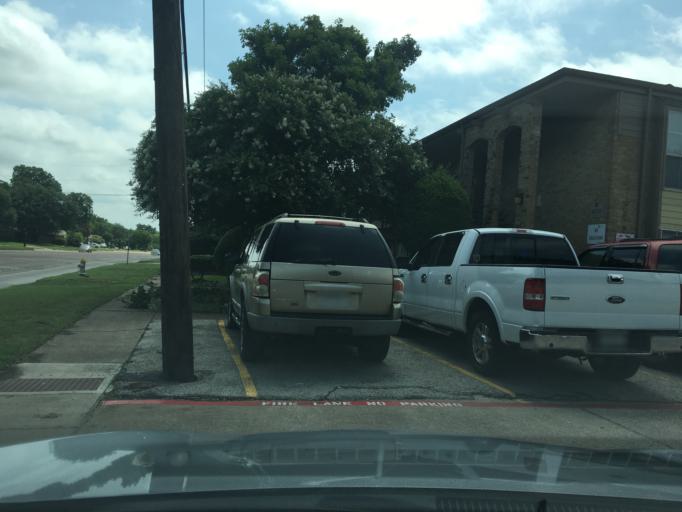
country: US
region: Texas
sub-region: Dallas County
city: Garland
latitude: 32.9164
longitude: -96.6746
